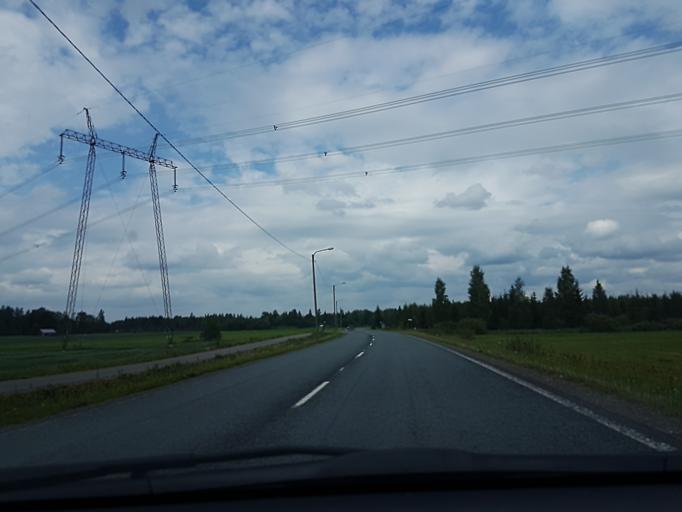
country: FI
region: Uusimaa
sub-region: Helsinki
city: Jaervenpaeae
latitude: 60.5157
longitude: 25.1017
